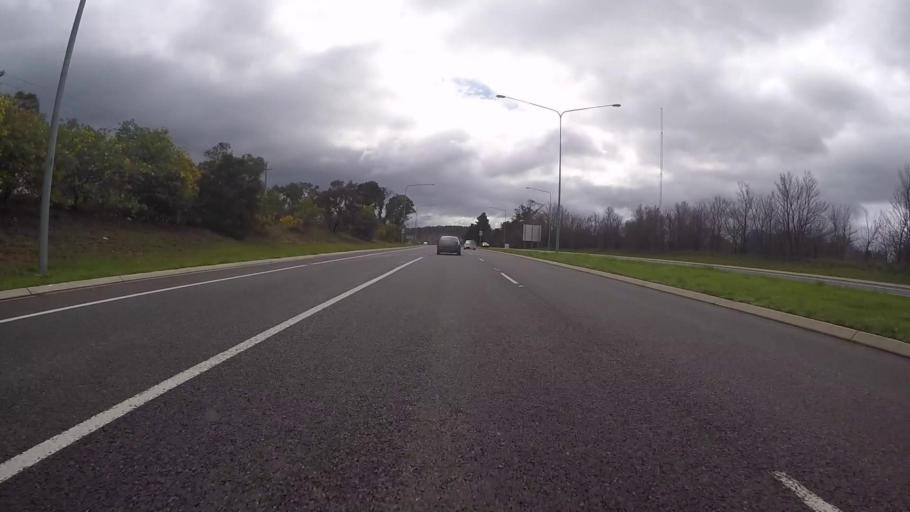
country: AU
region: Australian Capital Territory
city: Kaleen
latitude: -35.2217
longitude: 149.1204
